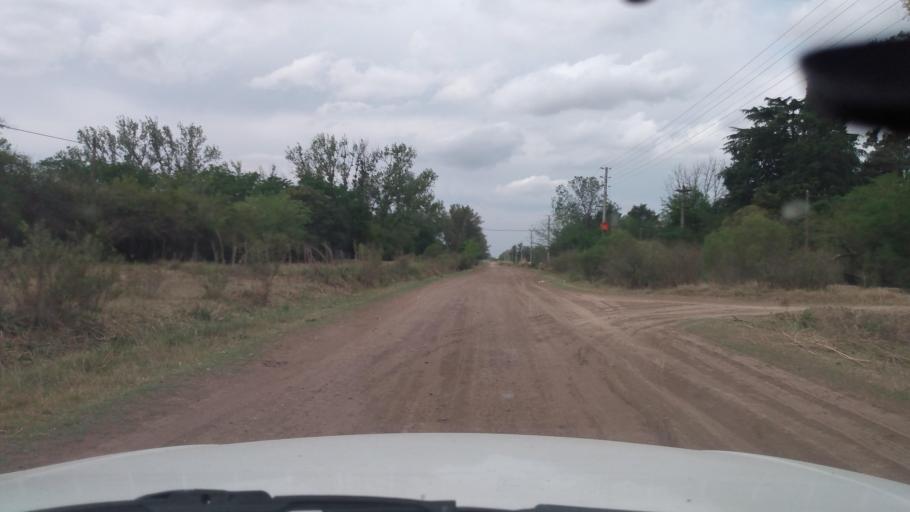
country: AR
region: Buenos Aires
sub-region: Partido de Lujan
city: Lujan
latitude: -34.5572
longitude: -59.1812
